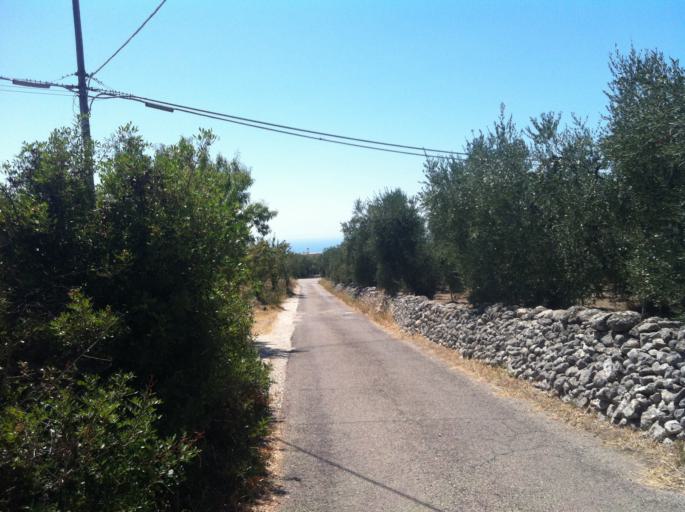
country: IT
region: Apulia
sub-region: Provincia di Foggia
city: Monte Sant'Angelo
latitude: 41.6610
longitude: 15.9465
